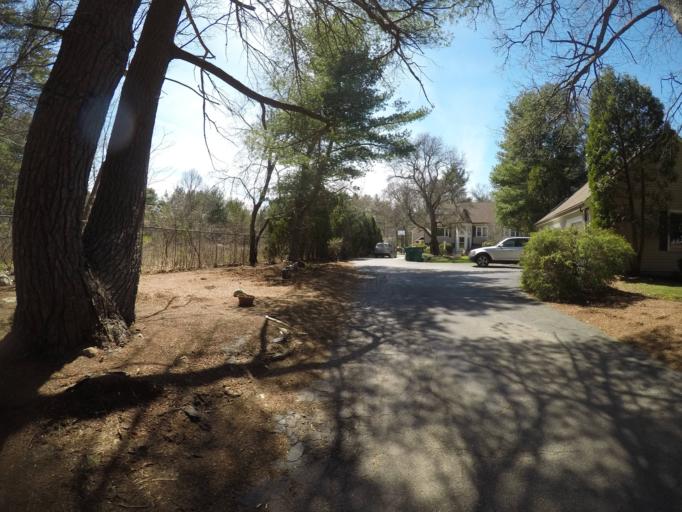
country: US
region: Massachusetts
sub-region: Bristol County
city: Easton
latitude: 42.0386
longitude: -71.0841
